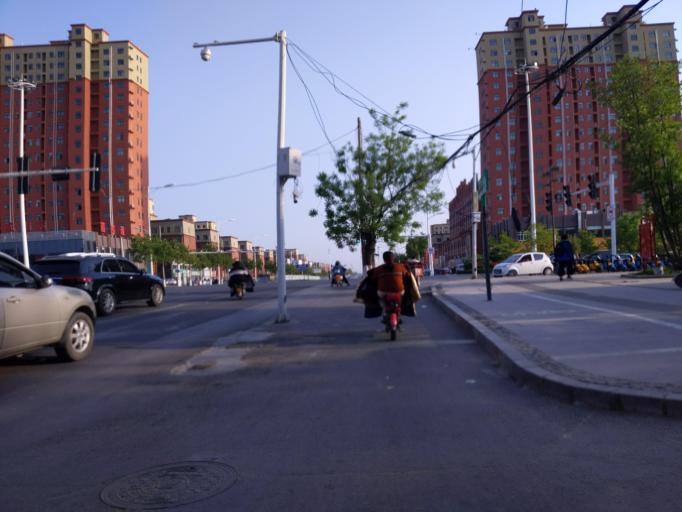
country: CN
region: Henan Sheng
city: Puyang Chengguanzhen
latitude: 35.6987
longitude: 115.0160
